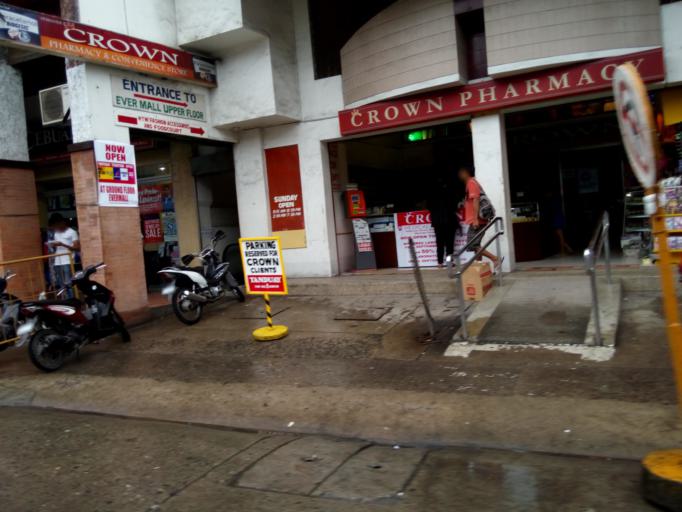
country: PH
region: Central Visayas
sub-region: Province of Negros Oriental
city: Dumaguete
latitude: 9.3089
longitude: 123.3075
